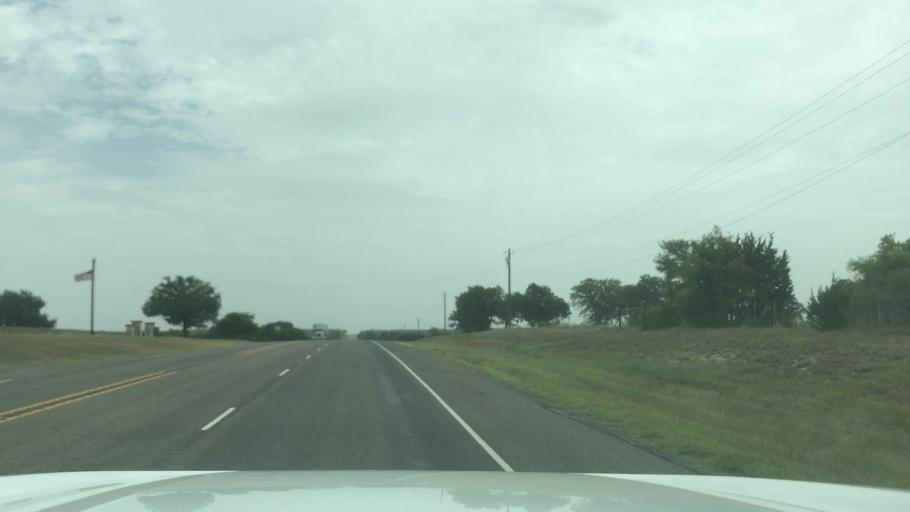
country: US
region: Texas
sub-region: Hamilton County
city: Hico
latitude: 31.9808
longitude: -98.0164
